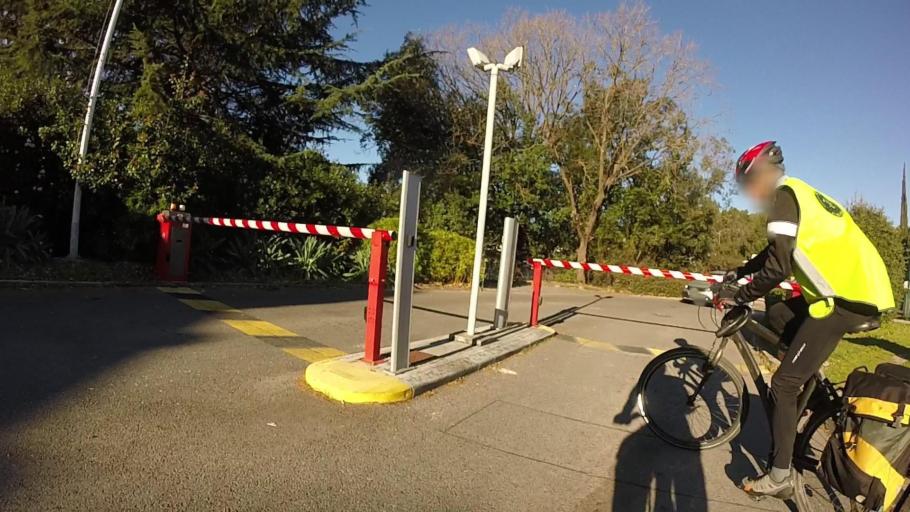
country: FR
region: Provence-Alpes-Cote d'Azur
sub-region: Departement des Alpes-Maritimes
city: Biot
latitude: 43.5880
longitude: 7.0927
